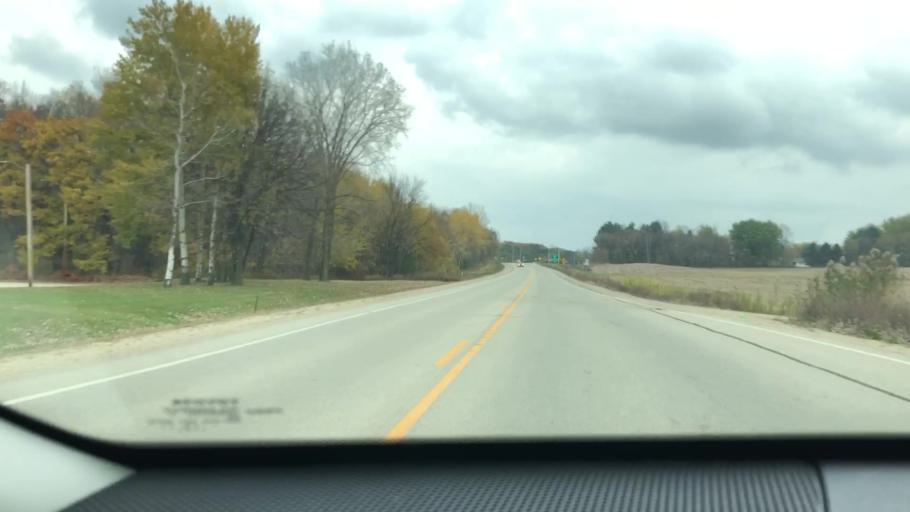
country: US
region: Wisconsin
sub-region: Brown County
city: Oneida
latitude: 44.4987
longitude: -88.1558
